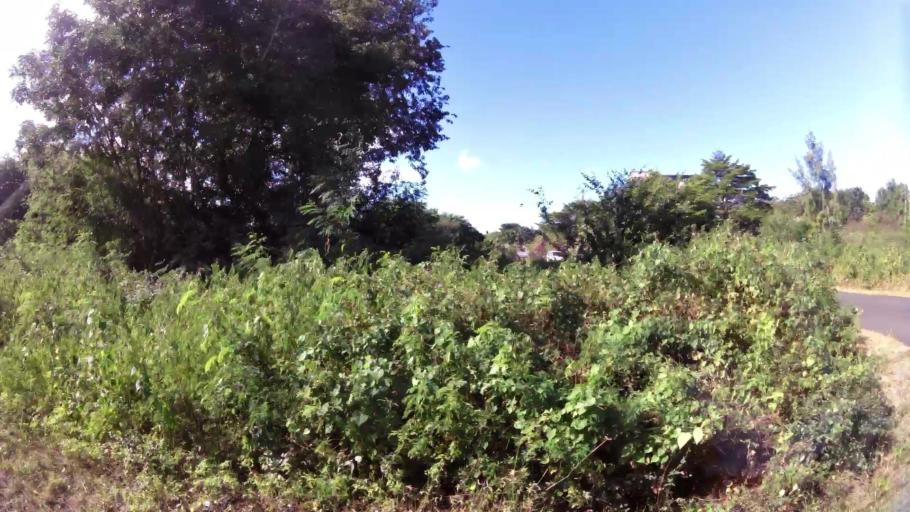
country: MU
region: Black River
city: Albion
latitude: -20.2038
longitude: 57.4057
